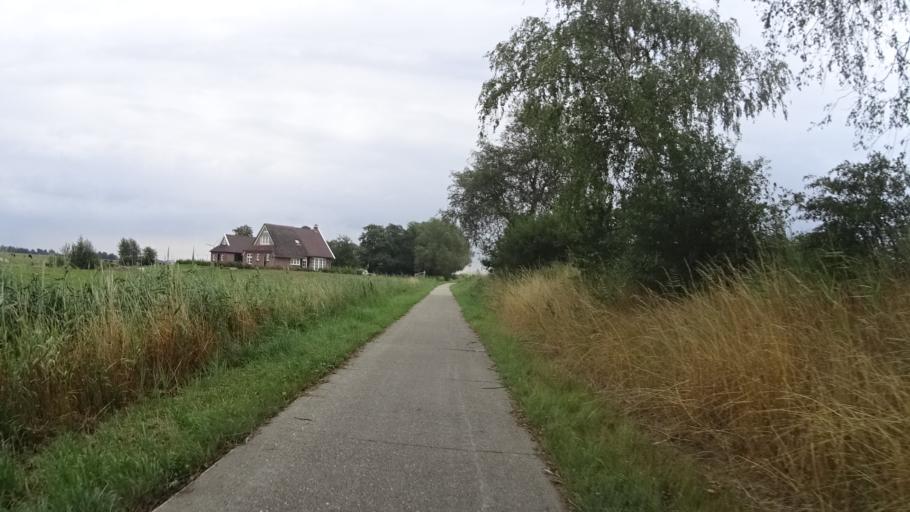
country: NL
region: Groningen
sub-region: Gemeente Hoogezand-Sappemeer
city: Hoogezand
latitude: 53.2354
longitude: 6.7158
